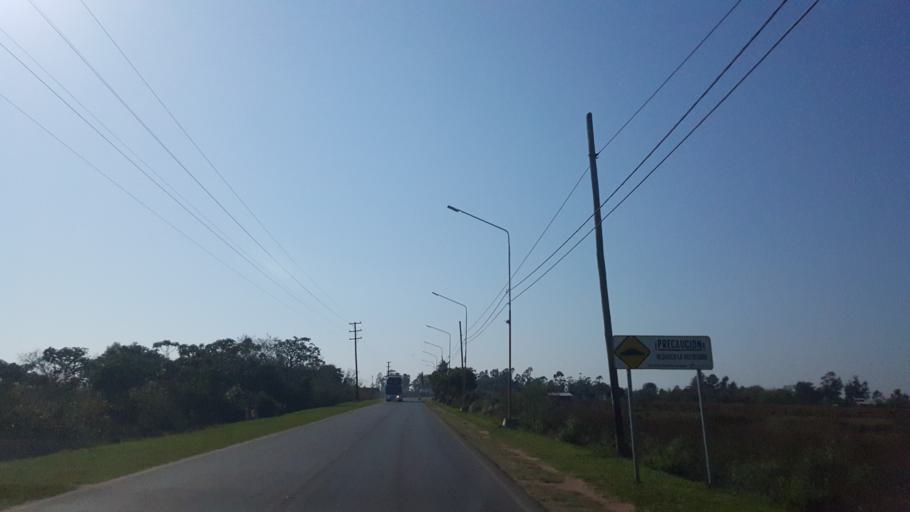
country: AR
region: Corrientes
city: Ituzaingo
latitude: -27.5938
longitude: -56.6825
